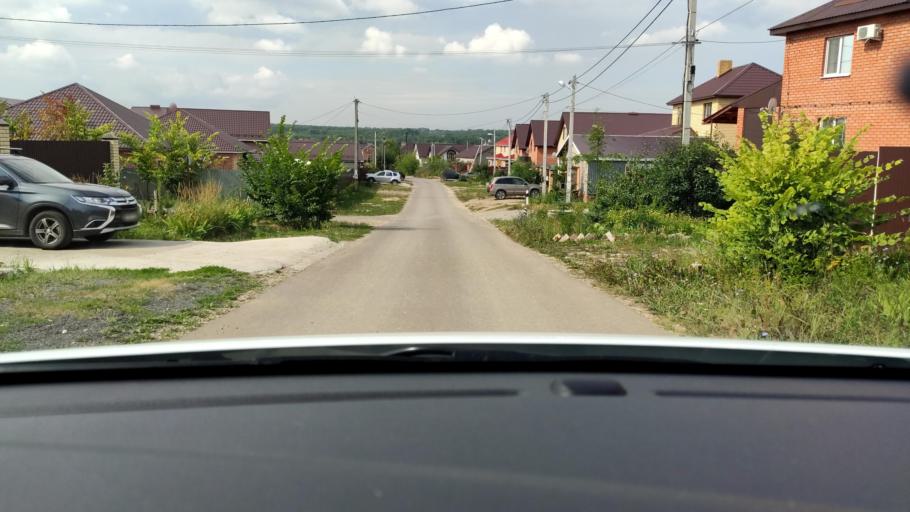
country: RU
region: Tatarstan
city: Stolbishchi
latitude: 55.7545
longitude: 49.2743
